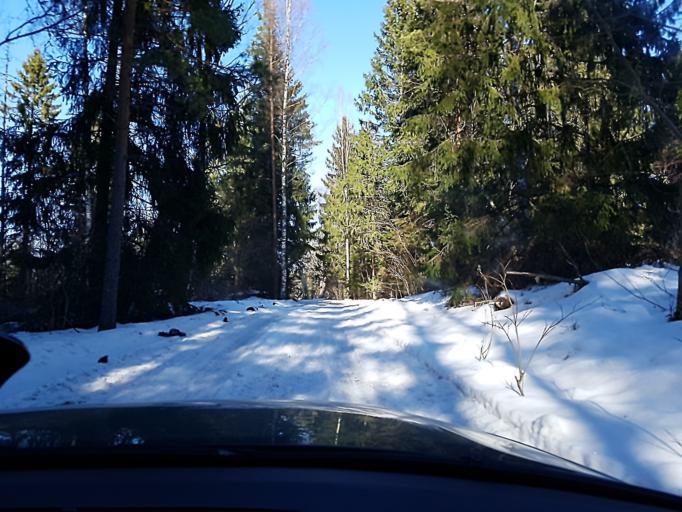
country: FI
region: Uusimaa
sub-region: Helsinki
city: Karjalohja
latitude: 60.2036
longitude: 23.7040
